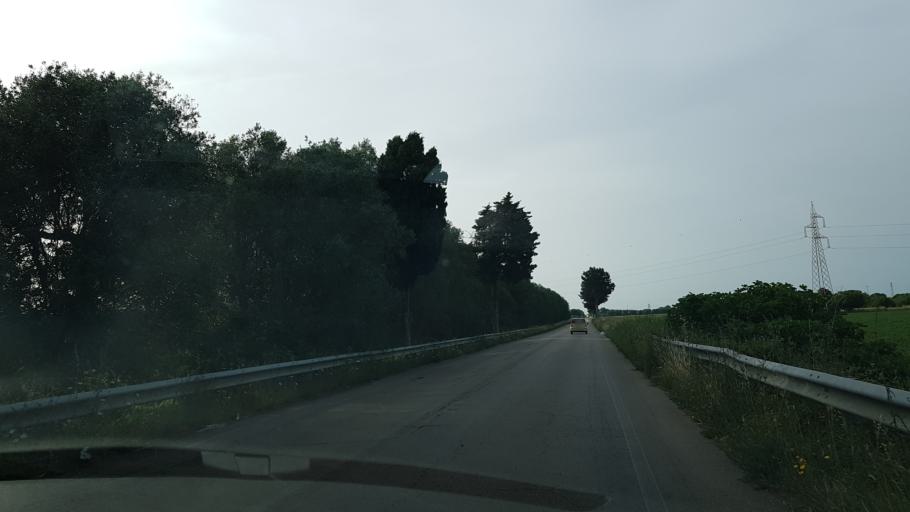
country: IT
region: Apulia
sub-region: Provincia di Brindisi
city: Tuturano
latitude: 40.5352
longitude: 17.9811
